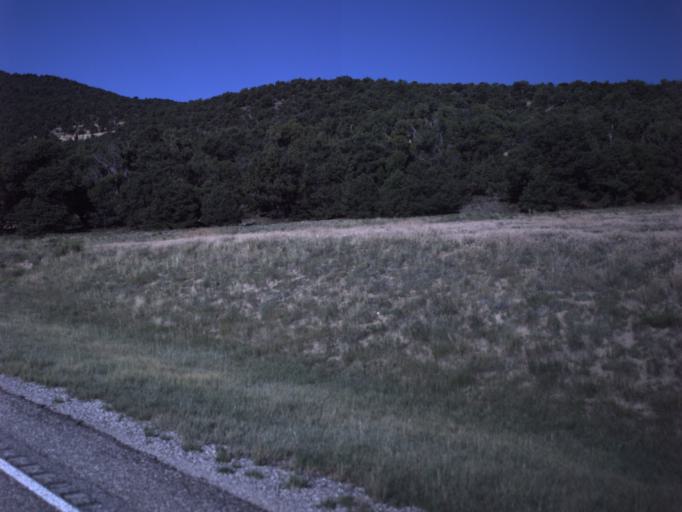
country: US
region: Utah
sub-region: Wayne County
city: Loa
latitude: 38.7478
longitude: -111.3918
